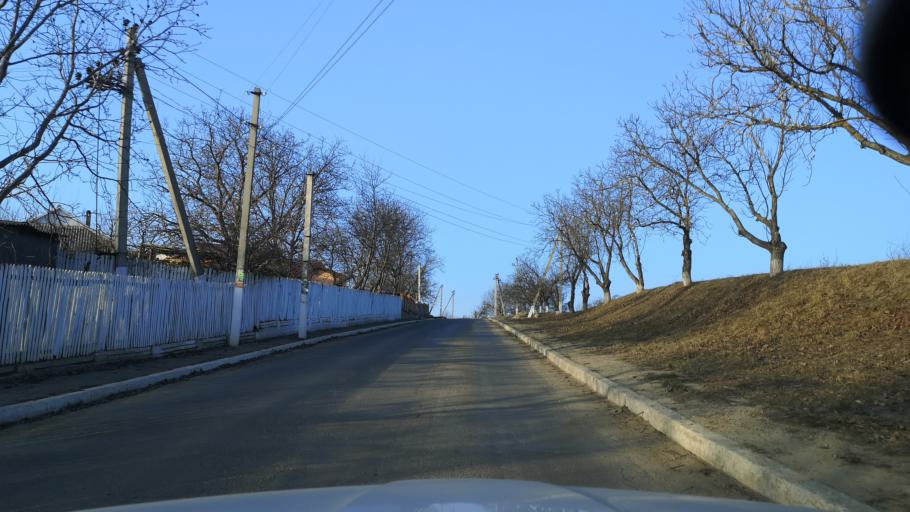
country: MD
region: Stinga Nistrului
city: Bucovat
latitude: 47.1219
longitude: 28.5038
